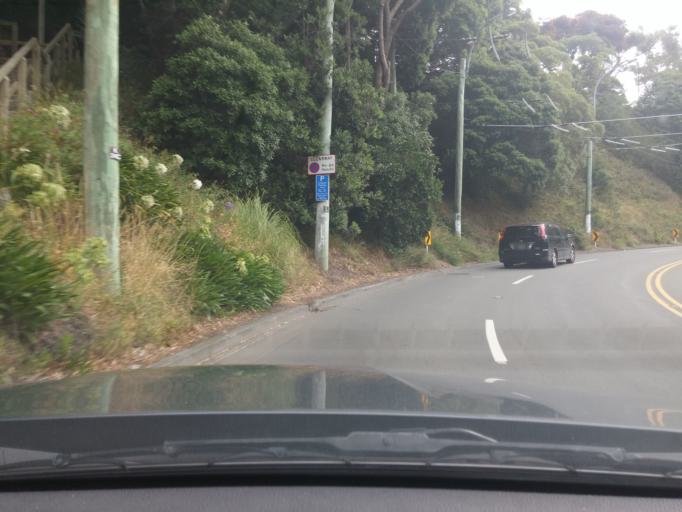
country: NZ
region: Wellington
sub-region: Wellington City
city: Kelburn
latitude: -41.2793
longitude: 174.7714
